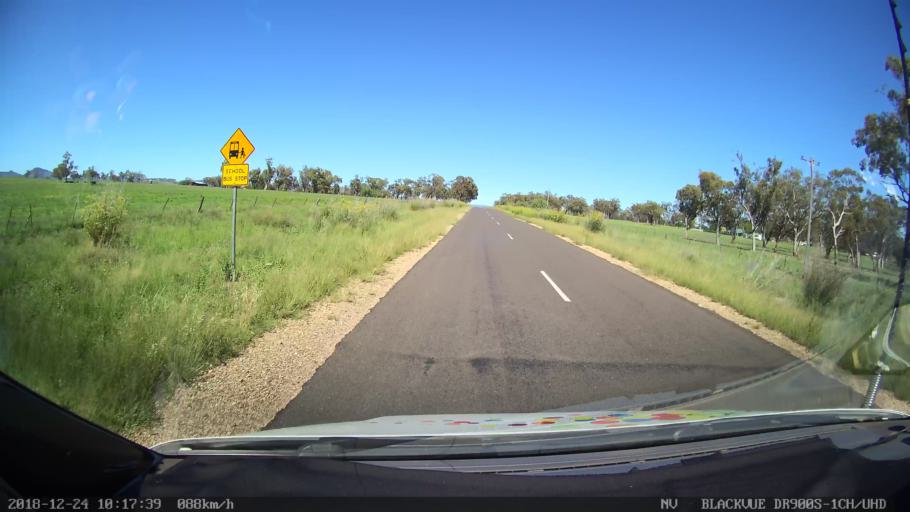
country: AU
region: New South Wales
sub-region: Liverpool Plains
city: Quirindi
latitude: -31.7209
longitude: 150.5880
